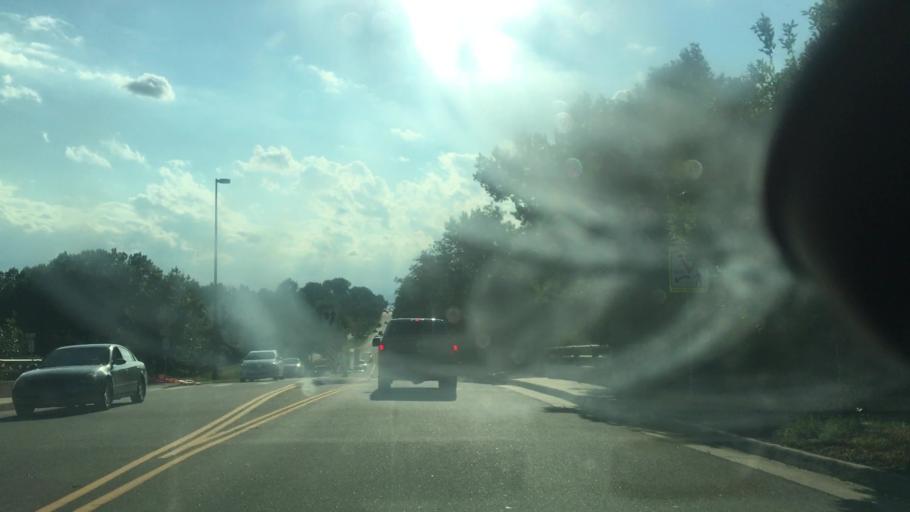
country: US
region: Colorado
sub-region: Arapahoe County
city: Glendale
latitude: 39.6675
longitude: -104.9044
